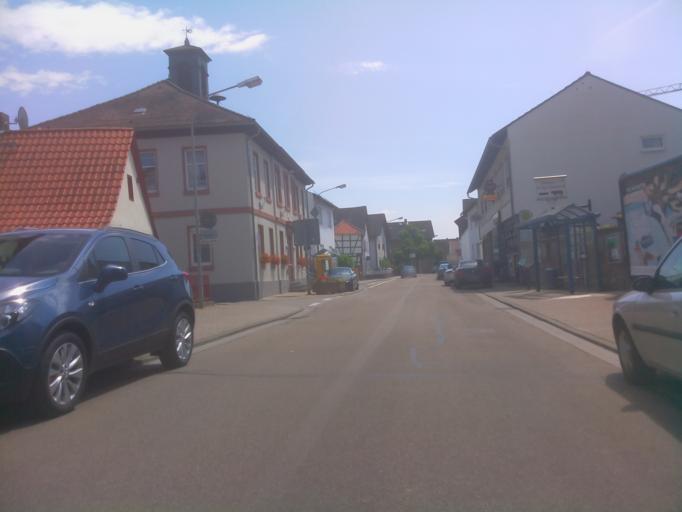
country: DE
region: Hesse
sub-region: Regierungsbezirk Darmstadt
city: Einhausen
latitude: 49.6980
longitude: 8.5670
